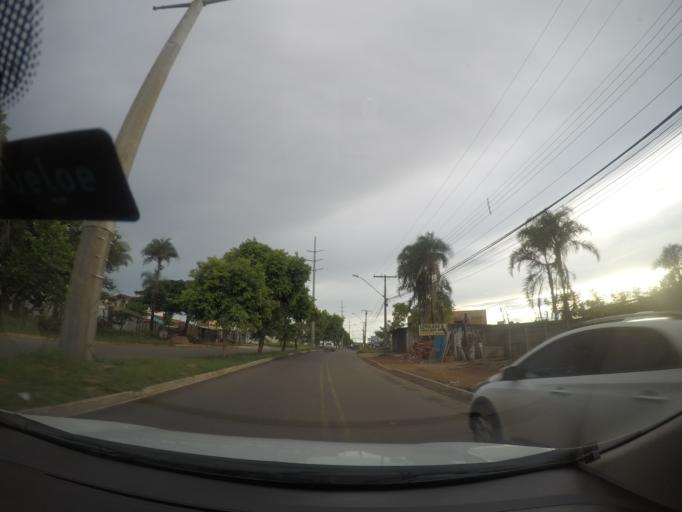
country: BR
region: Goias
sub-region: Goiania
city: Goiania
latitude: -16.7346
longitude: -49.3098
